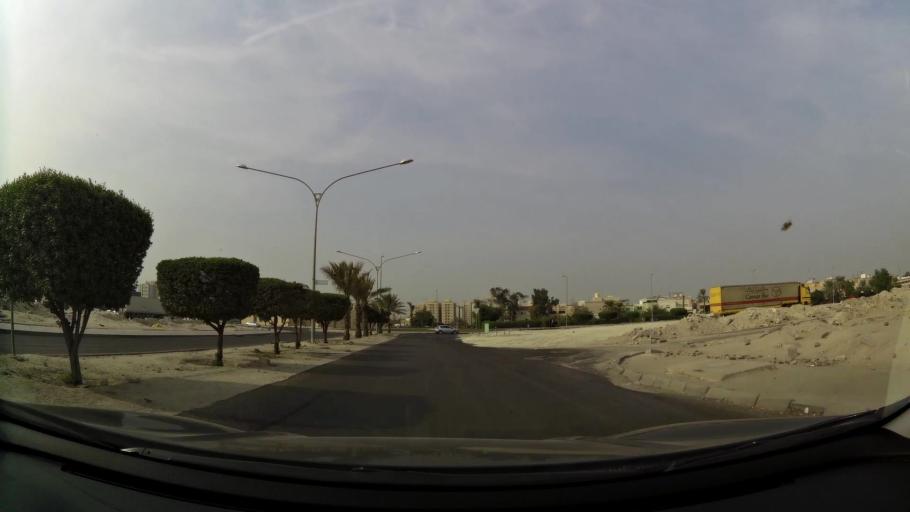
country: KW
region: Al Farwaniyah
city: Janub as Surrah
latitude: 29.2761
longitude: 47.9783
